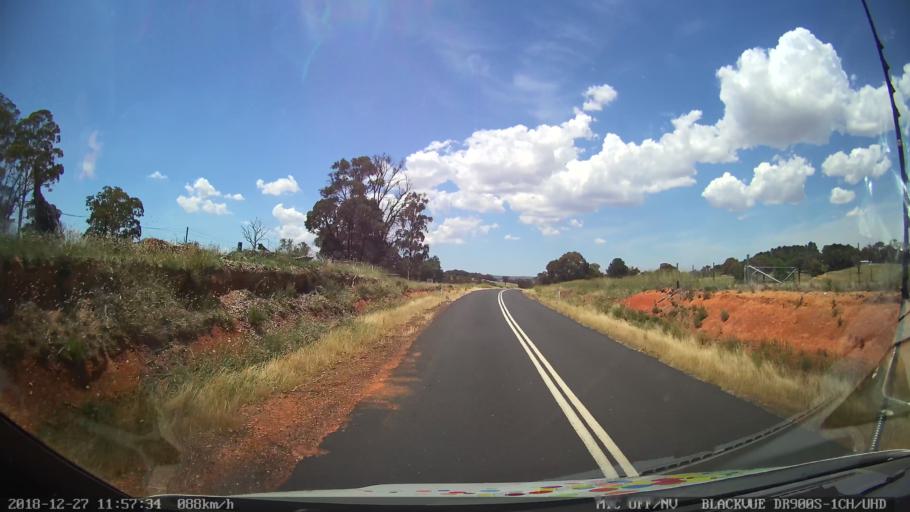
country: AU
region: New South Wales
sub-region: Blayney
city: Blayney
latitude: -33.7133
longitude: 149.3877
